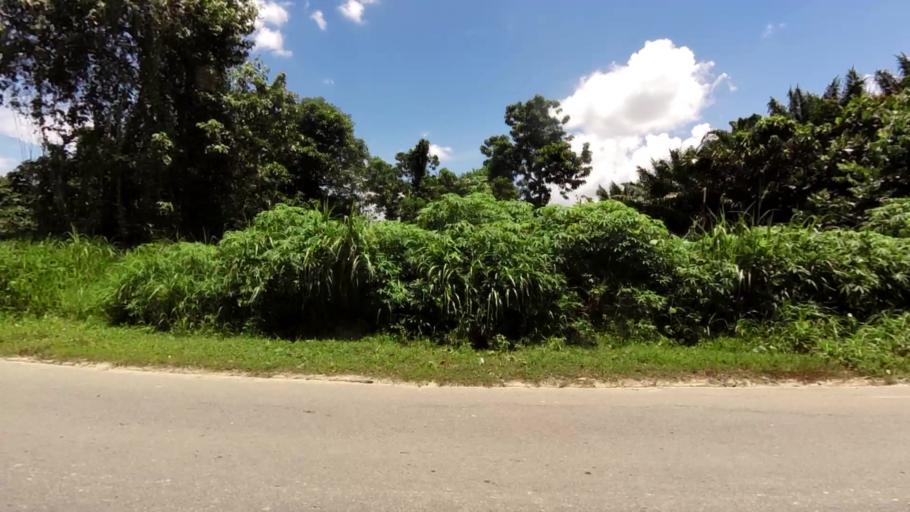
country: BN
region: Brunei and Muara
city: Bandar Seri Begawan
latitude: 4.9383
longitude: 114.9591
